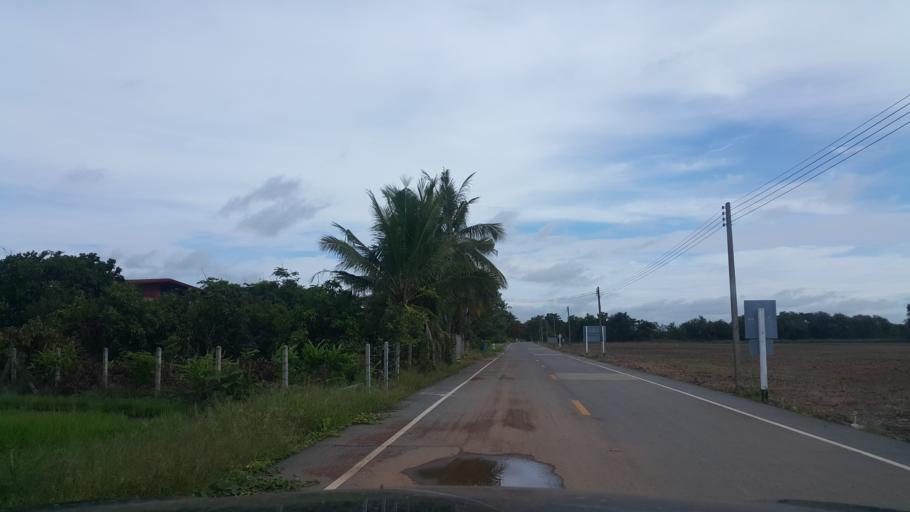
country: TH
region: Sukhothai
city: Si Nakhon
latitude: 17.2634
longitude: 99.9345
